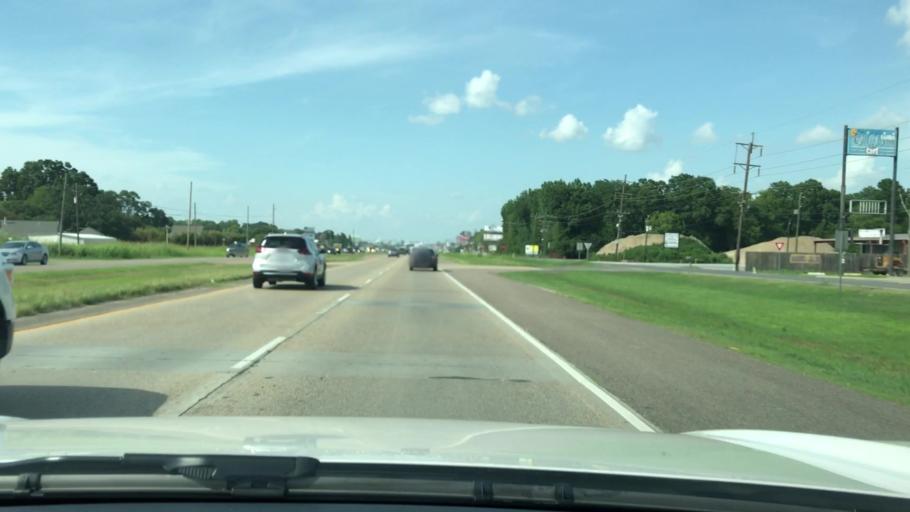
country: US
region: Louisiana
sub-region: West Baton Rouge Parish
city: Brusly
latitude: 30.4104
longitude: -91.2273
